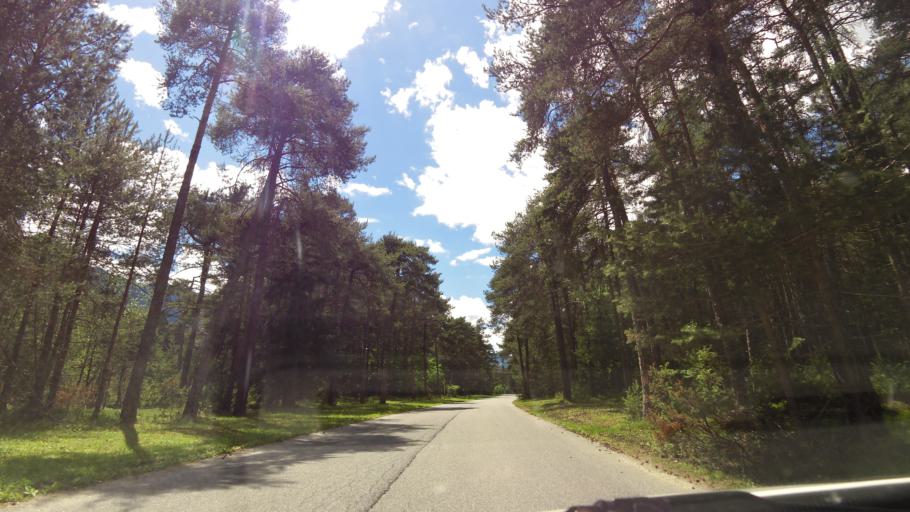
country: AT
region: Tyrol
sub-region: Politischer Bezirk Imst
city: Haiming
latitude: 47.2404
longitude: 10.8701
